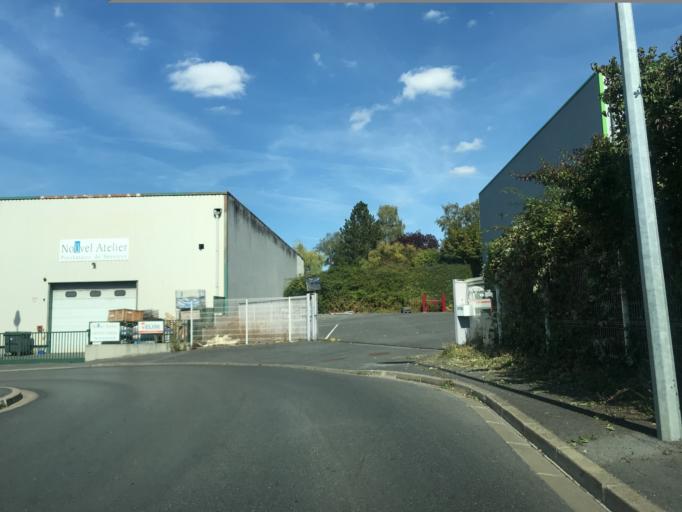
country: FR
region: Champagne-Ardenne
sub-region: Departement de la Marne
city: Pierry
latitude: 49.0275
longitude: 3.9516
